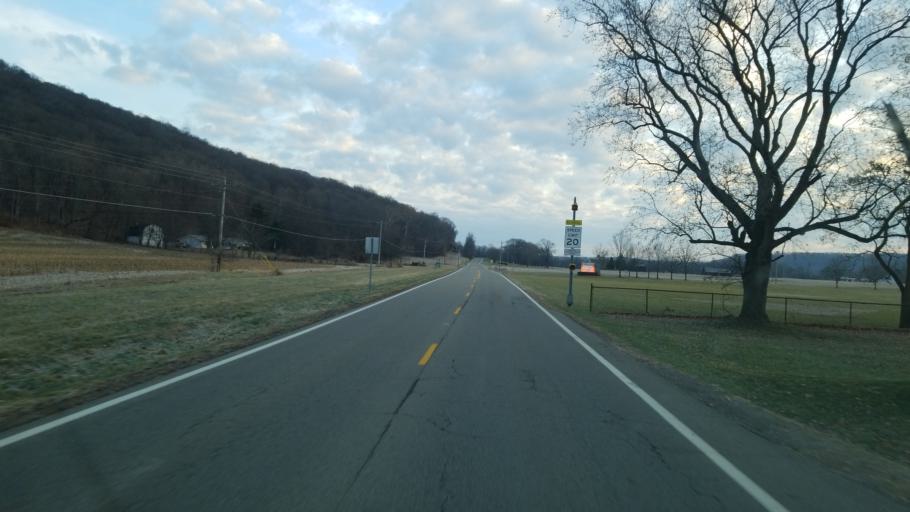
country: US
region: Ohio
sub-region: Ross County
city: Frankfort
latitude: 39.2439
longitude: -83.2164
